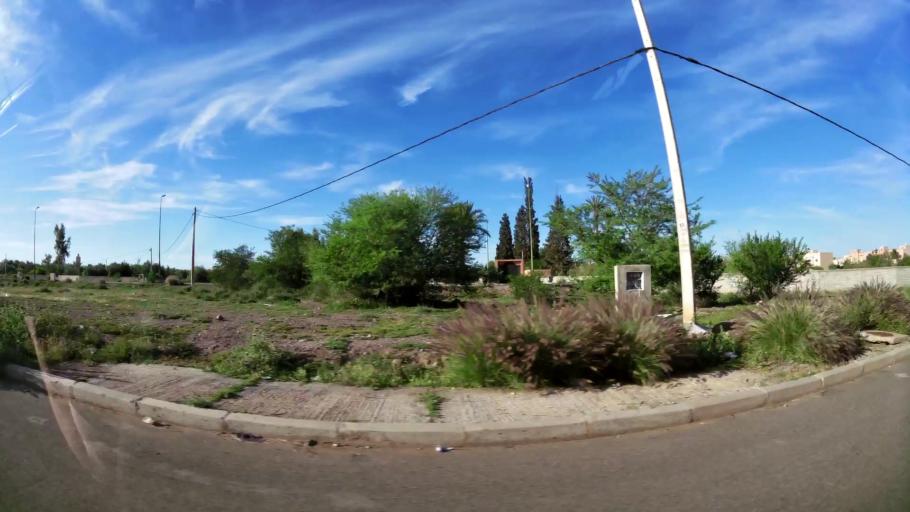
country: MA
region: Marrakech-Tensift-Al Haouz
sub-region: Marrakech
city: Marrakesh
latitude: 31.6790
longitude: -8.0665
